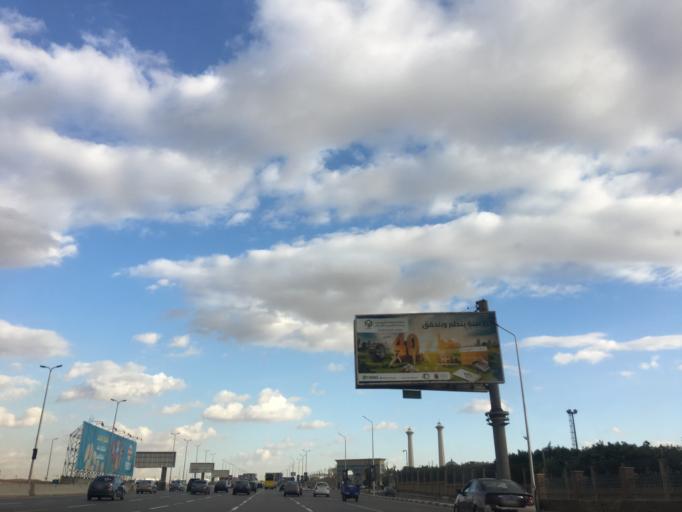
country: EG
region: Muhafazat al Qahirah
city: Cairo
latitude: 30.0208
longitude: 31.3765
